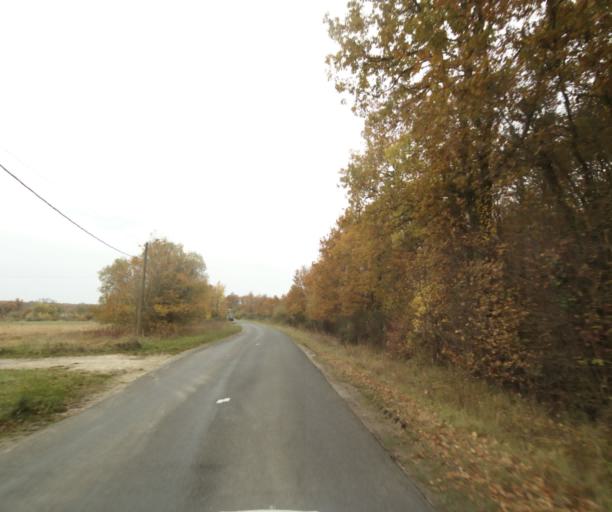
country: FR
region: Poitou-Charentes
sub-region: Departement de la Charente-Maritime
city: Chermignac
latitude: 45.7152
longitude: -0.6937
